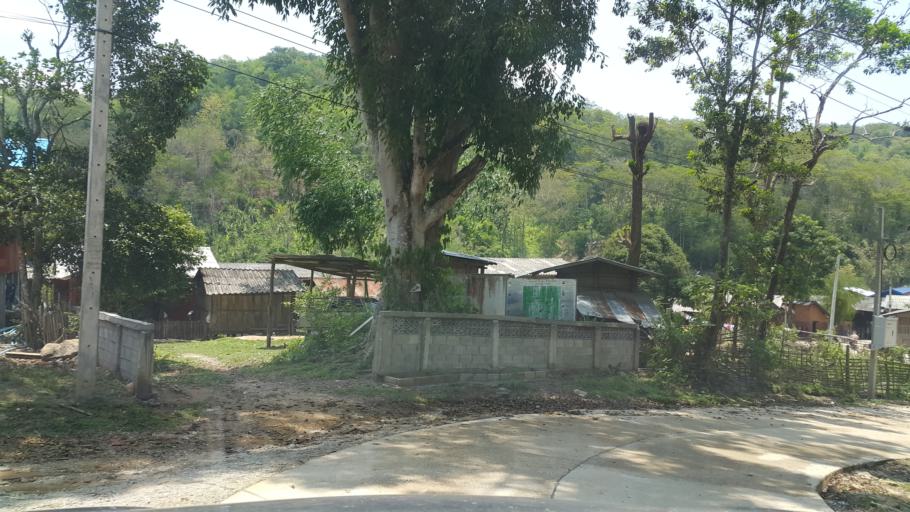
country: TH
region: Chiang Rai
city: Chiang Rai
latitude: 20.0008
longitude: 99.7217
